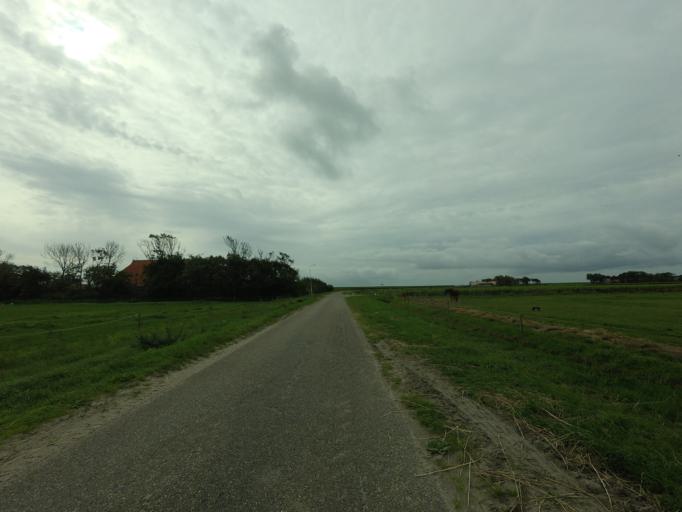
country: NL
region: Friesland
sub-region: Gemeente Ameland
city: Nes
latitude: 53.4366
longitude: 5.7066
